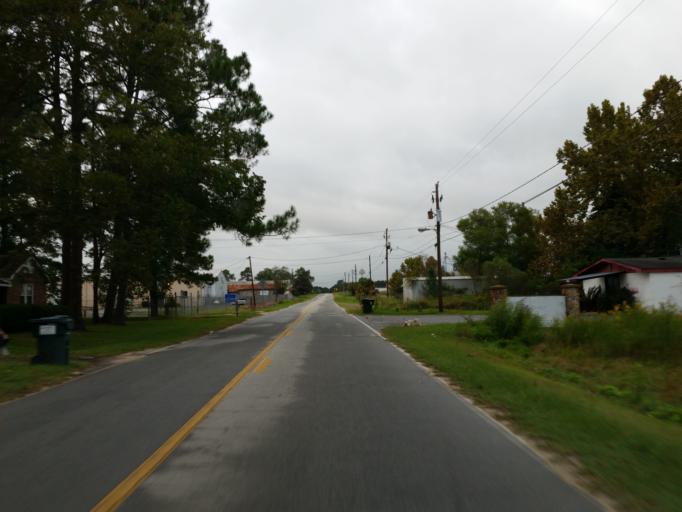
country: US
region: Georgia
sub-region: Turner County
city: Ashburn
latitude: 31.6773
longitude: -83.6363
